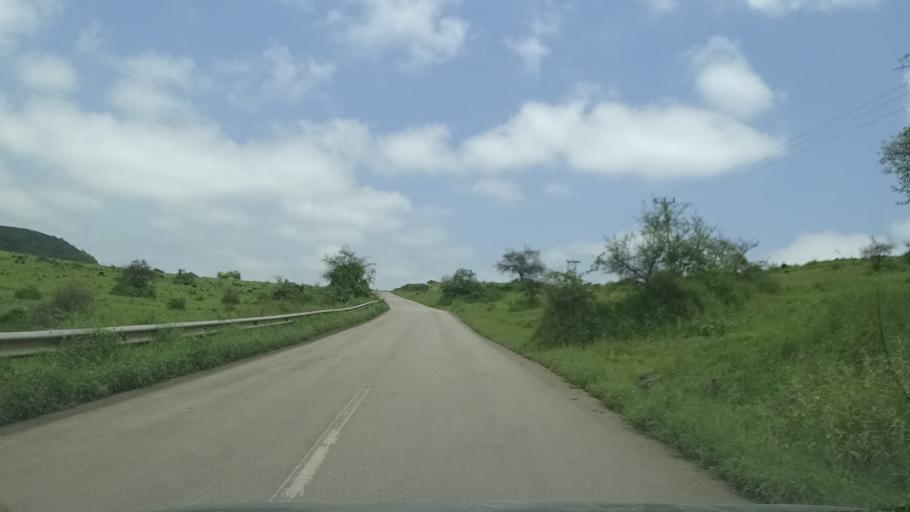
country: OM
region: Zufar
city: Salalah
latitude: 17.2020
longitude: 54.1852
